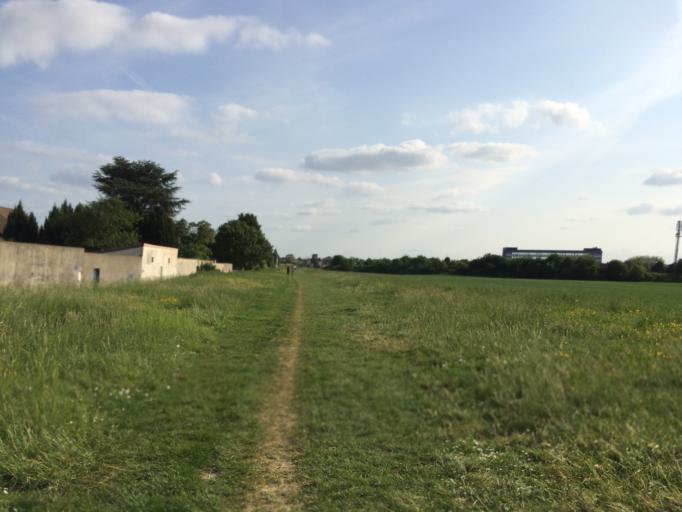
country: FR
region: Ile-de-France
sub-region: Departement de l'Essonne
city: Paray-Vieille-Poste
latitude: 48.7091
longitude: 2.3538
